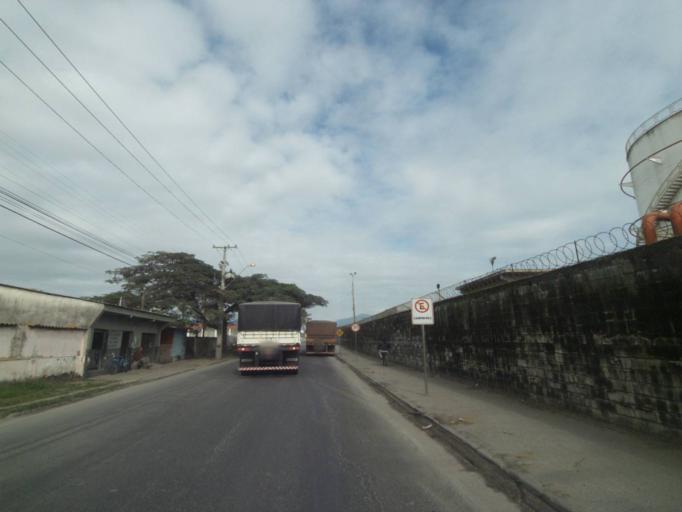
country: BR
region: Parana
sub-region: Paranagua
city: Paranagua
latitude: -25.5133
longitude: -48.5259
